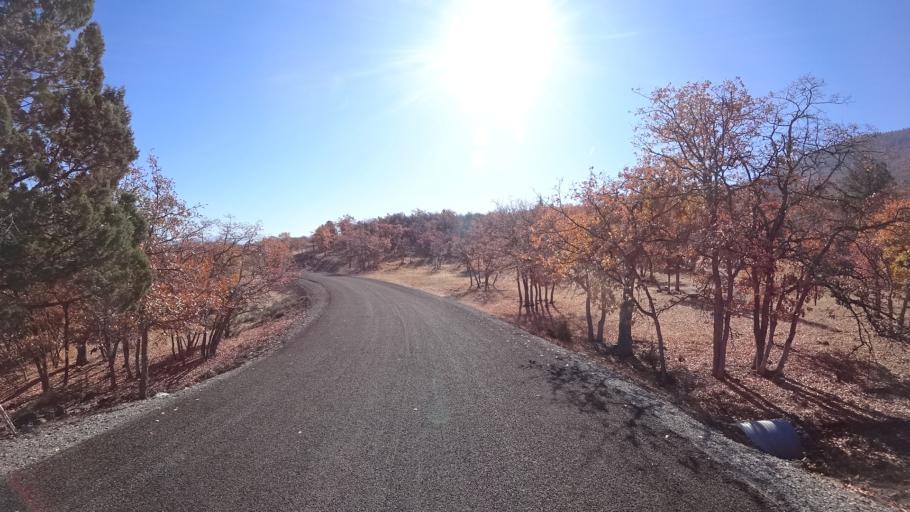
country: US
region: California
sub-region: Siskiyou County
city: Montague
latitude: 41.8788
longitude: -122.4904
